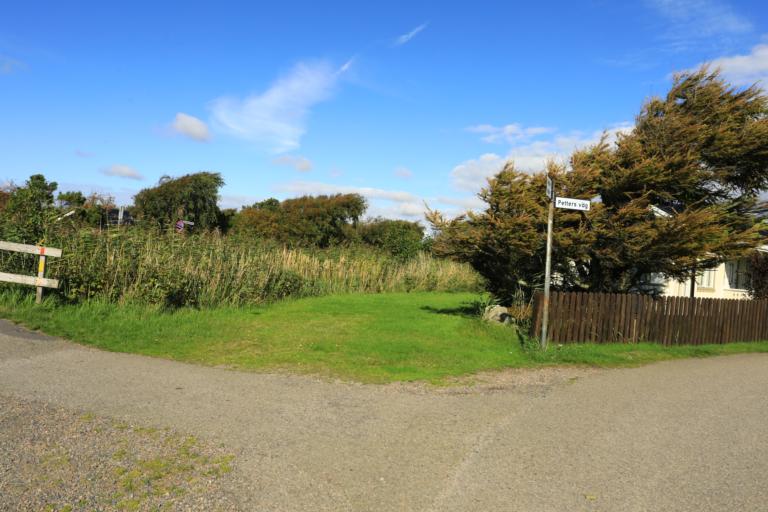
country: SE
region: Halland
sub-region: Varbergs Kommun
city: Traslovslage
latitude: 57.0768
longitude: 12.2637
